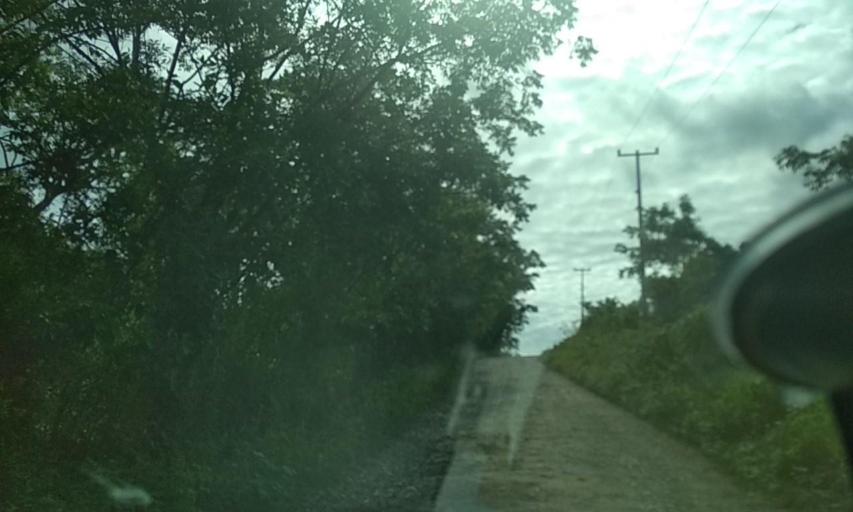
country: MX
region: Veracruz
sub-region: Papantla
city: Polutla
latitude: 20.5680
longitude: -97.1951
